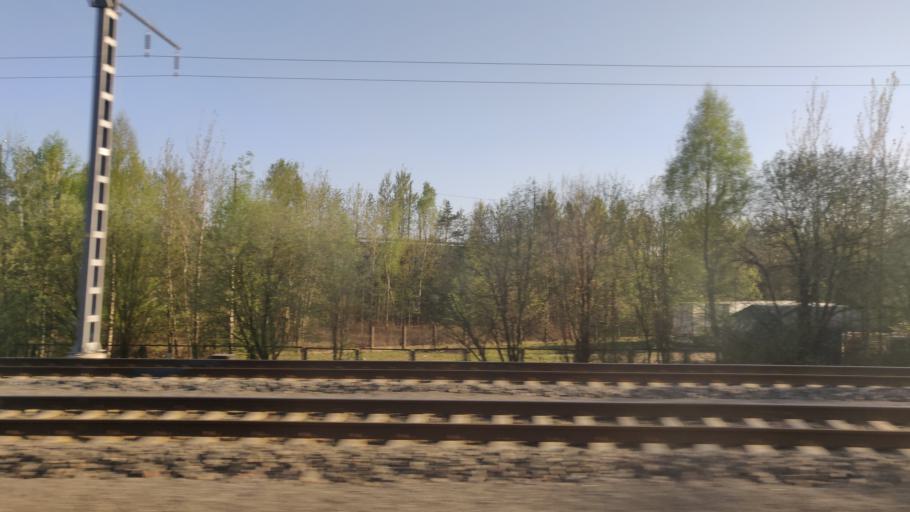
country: LT
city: Baltoji Voke
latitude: 54.6317
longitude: 25.1421
